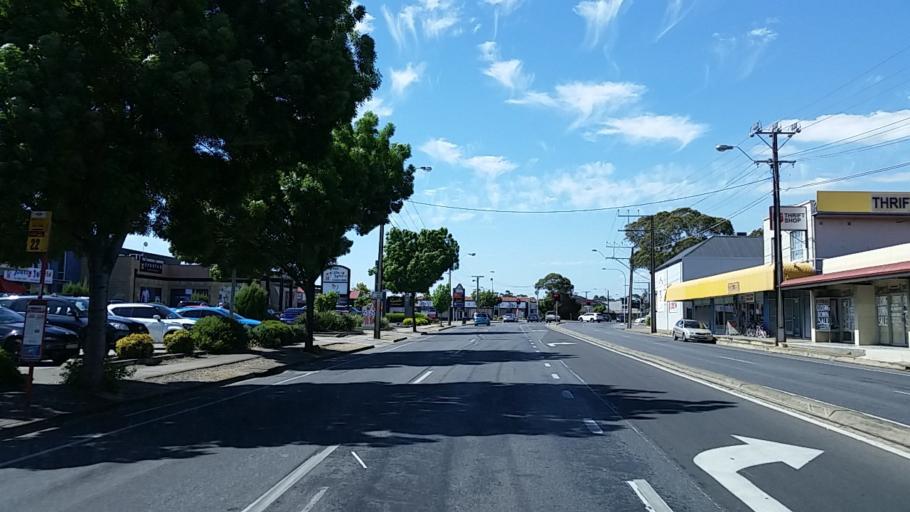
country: AU
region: South Australia
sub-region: Campbelltown
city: Campbelltown
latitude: -34.8777
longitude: 138.6639
